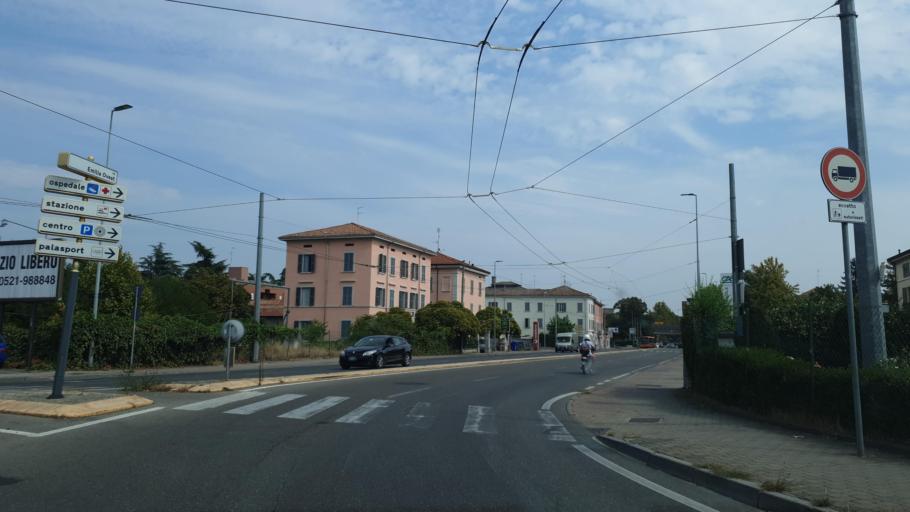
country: IT
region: Emilia-Romagna
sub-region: Provincia di Parma
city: Parma
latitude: 44.8071
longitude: 10.3000
